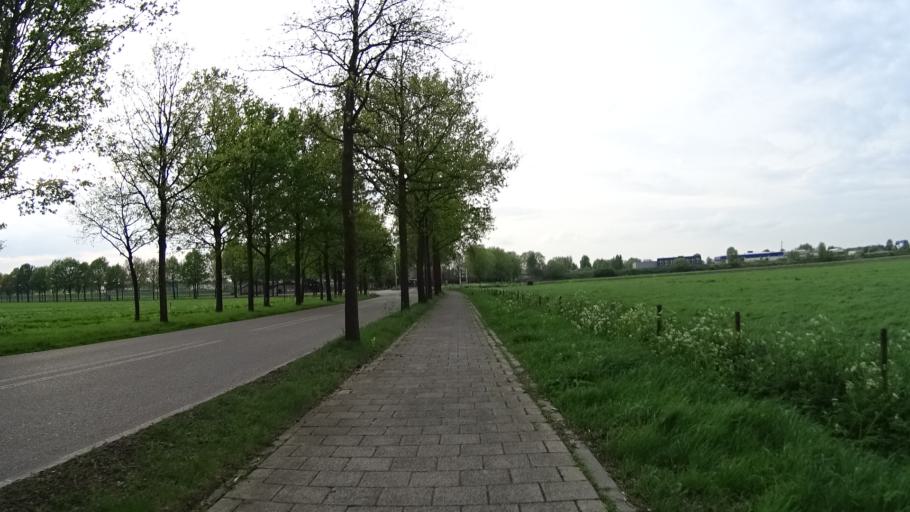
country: NL
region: North Brabant
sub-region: Gemeente Heusden
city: Heusden
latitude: 51.7337
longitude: 5.1538
